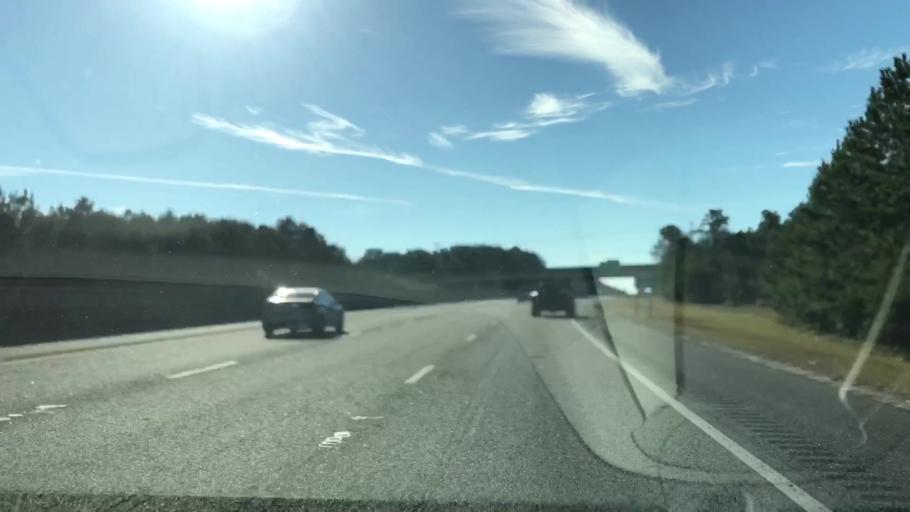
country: US
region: South Carolina
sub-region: Berkeley County
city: Ladson
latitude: 32.9813
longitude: -80.0778
